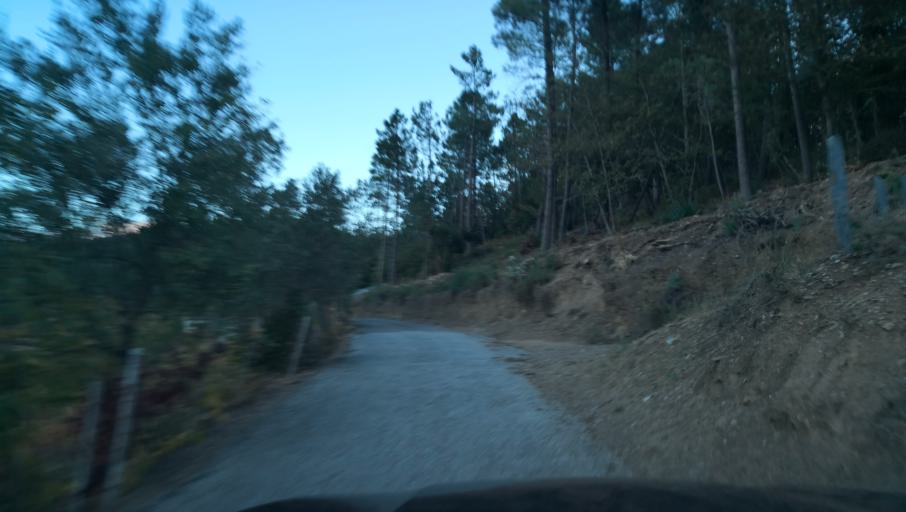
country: PT
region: Vila Real
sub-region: Santa Marta de Penaguiao
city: Santa Marta de Penaguiao
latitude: 41.2644
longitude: -7.8287
